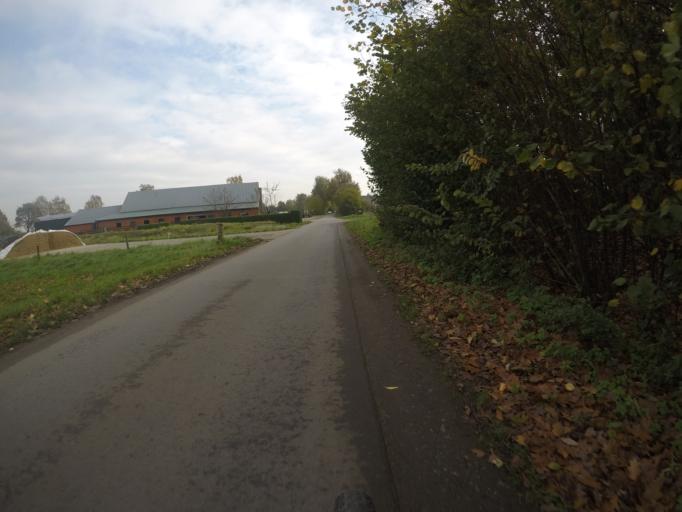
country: DE
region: North Rhine-Westphalia
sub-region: Regierungsbezirk Munster
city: Isselburg
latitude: 51.8345
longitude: 6.5382
